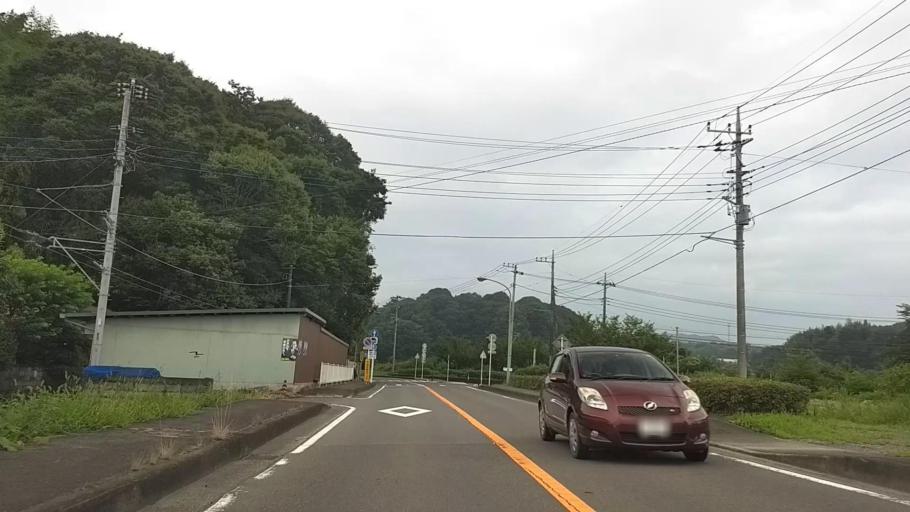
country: JP
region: Kanagawa
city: Hadano
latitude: 35.3316
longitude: 139.2148
